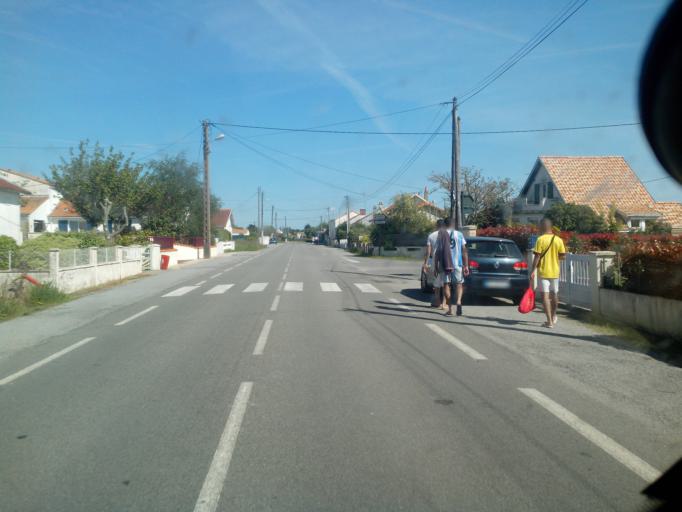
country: FR
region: Pays de la Loire
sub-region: Departement de la Loire-Atlantique
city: Pornic
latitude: 47.1068
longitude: -2.0761
